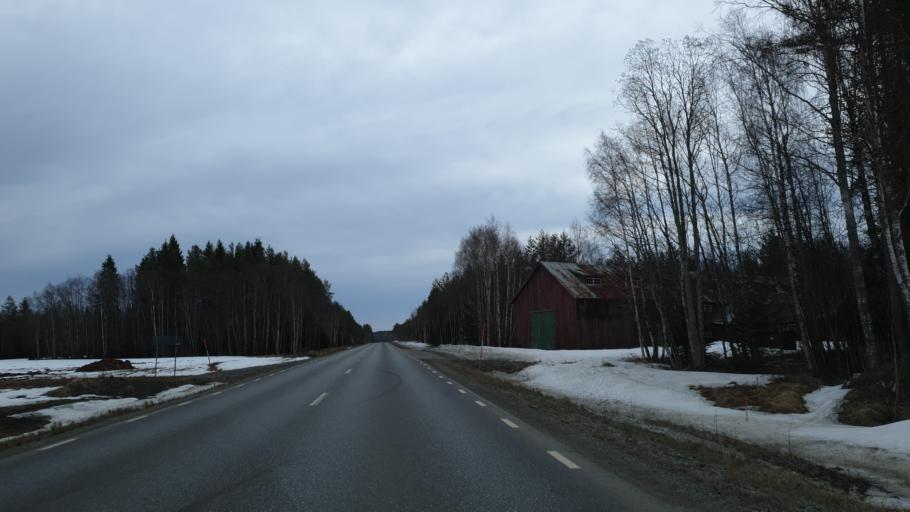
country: SE
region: Vaesterbotten
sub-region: Robertsfors Kommun
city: Robertsfors
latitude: 64.2327
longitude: 20.9738
